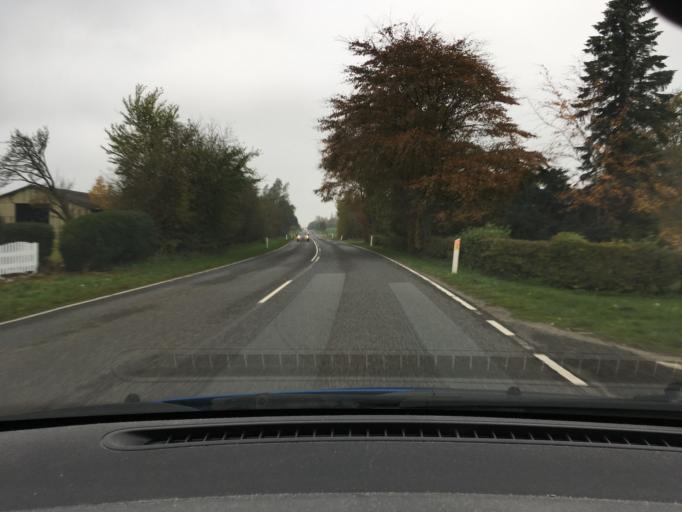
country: DK
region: South Denmark
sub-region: Tonder Kommune
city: Toftlund
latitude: 55.0679
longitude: 9.1599
